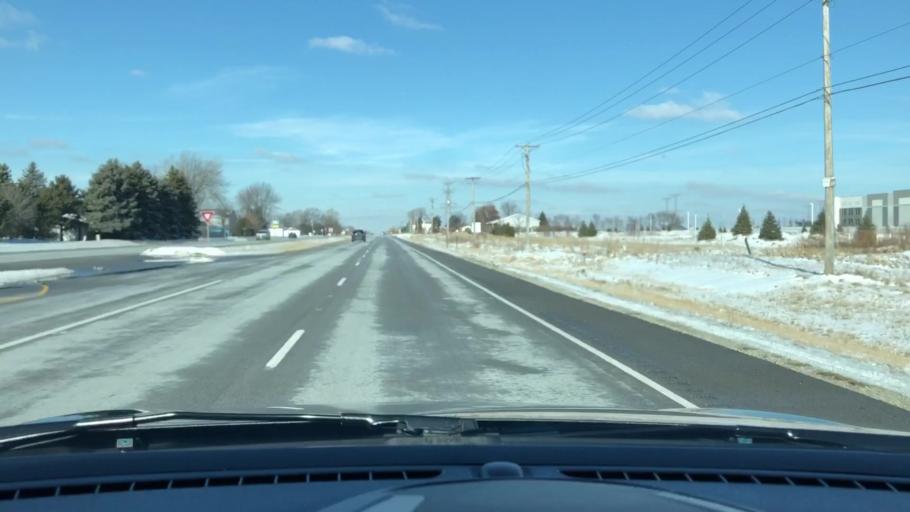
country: US
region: Illinois
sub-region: Will County
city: Preston Heights
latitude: 41.4477
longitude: -88.0789
